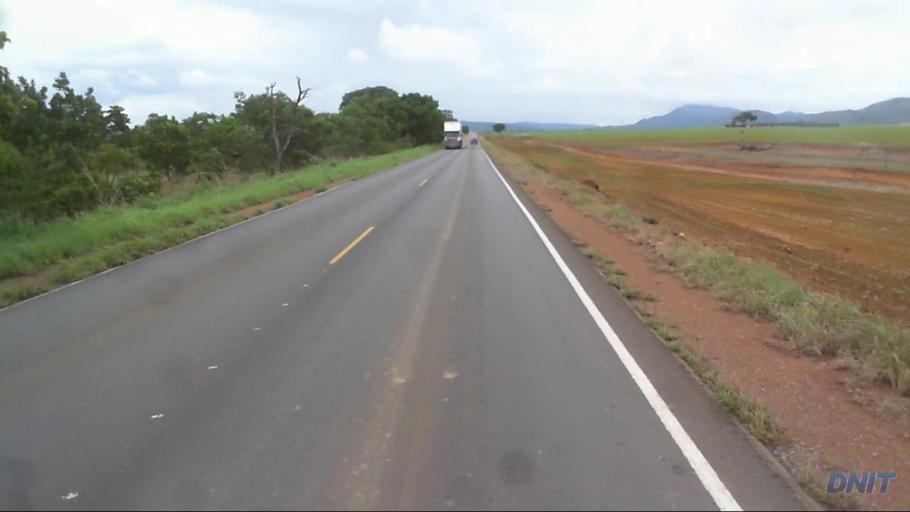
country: BR
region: Goias
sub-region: Padre Bernardo
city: Padre Bernardo
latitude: -15.3261
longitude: -48.2311
